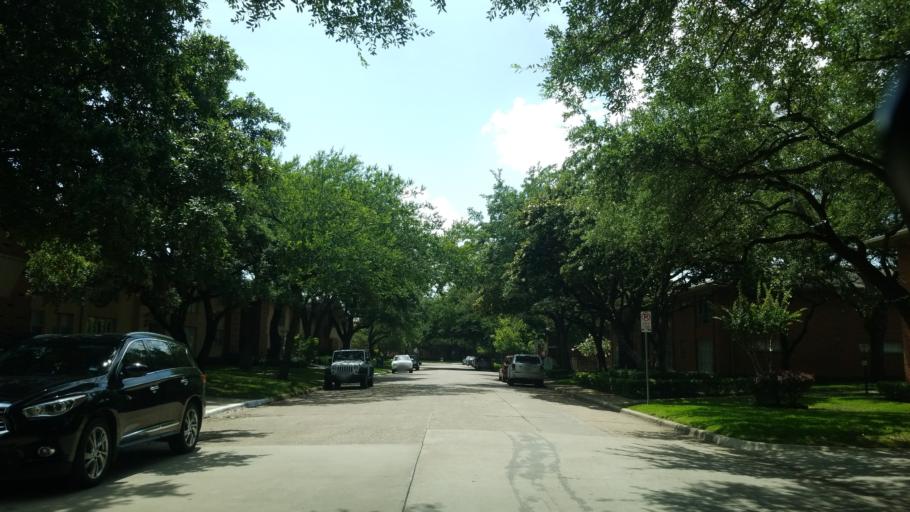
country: US
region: Texas
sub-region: Dallas County
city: University Park
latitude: 32.8675
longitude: -96.8010
